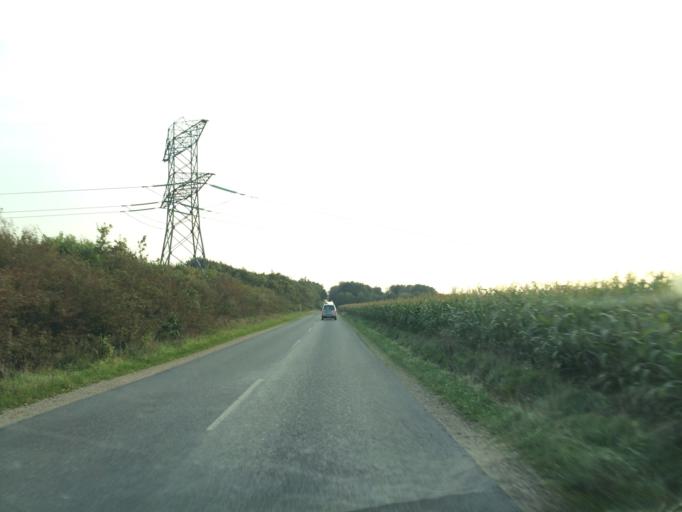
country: DK
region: Central Jutland
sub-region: Holstebro Kommune
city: Vinderup
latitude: 56.4080
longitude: 8.8337
